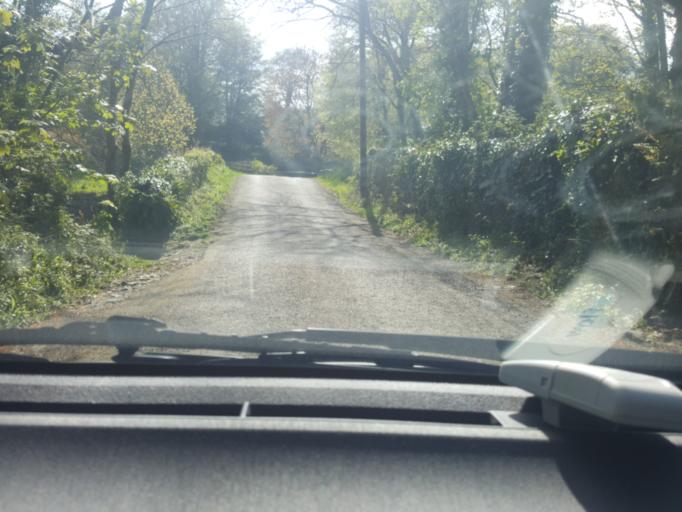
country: IE
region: Munster
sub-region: County Cork
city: Bandon
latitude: 51.7675
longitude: -8.6789
